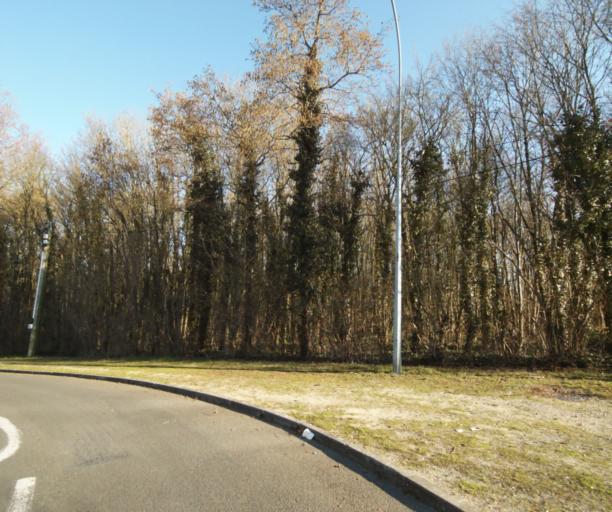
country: FR
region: Poitou-Charentes
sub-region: Departement des Deux-Sevres
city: Niort
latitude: 46.3370
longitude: -0.4382
